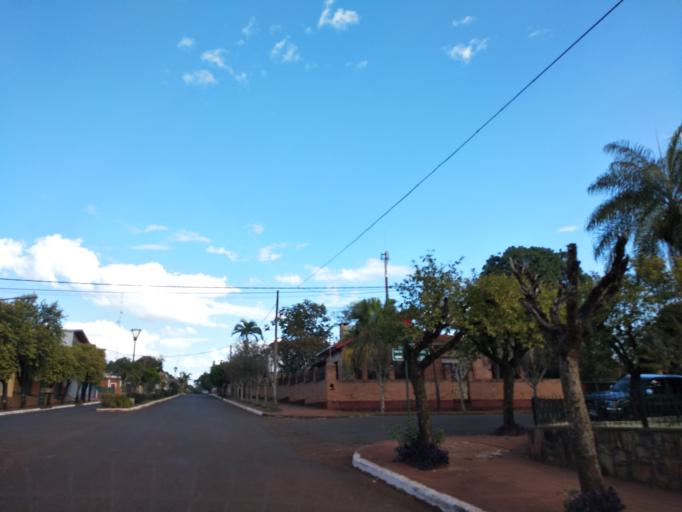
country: AR
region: Misiones
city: Jardin America
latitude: -27.0389
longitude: -55.2271
